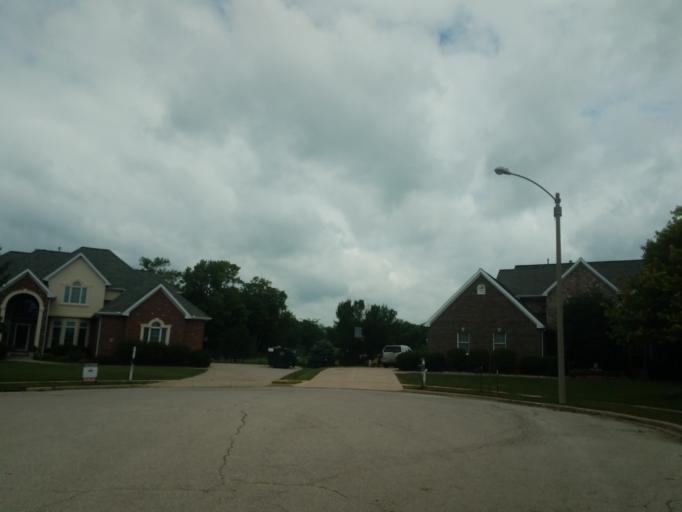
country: US
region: Illinois
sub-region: McLean County
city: Twin Grove
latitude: 40.4526
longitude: -89.0460
